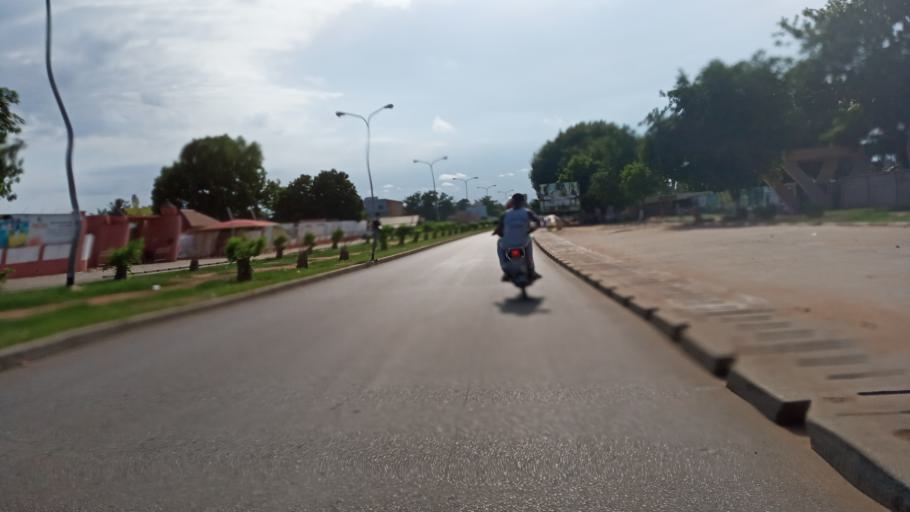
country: TG
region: Maritime
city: Lome
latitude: 6.1881
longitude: 1.2568
